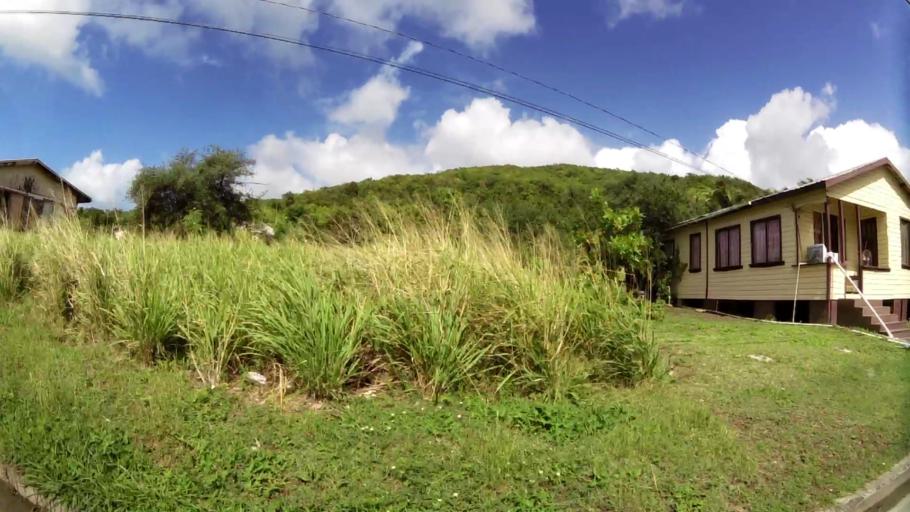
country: AG
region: Saint Mary
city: Bolands
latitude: 17.0782
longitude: -61.8669
